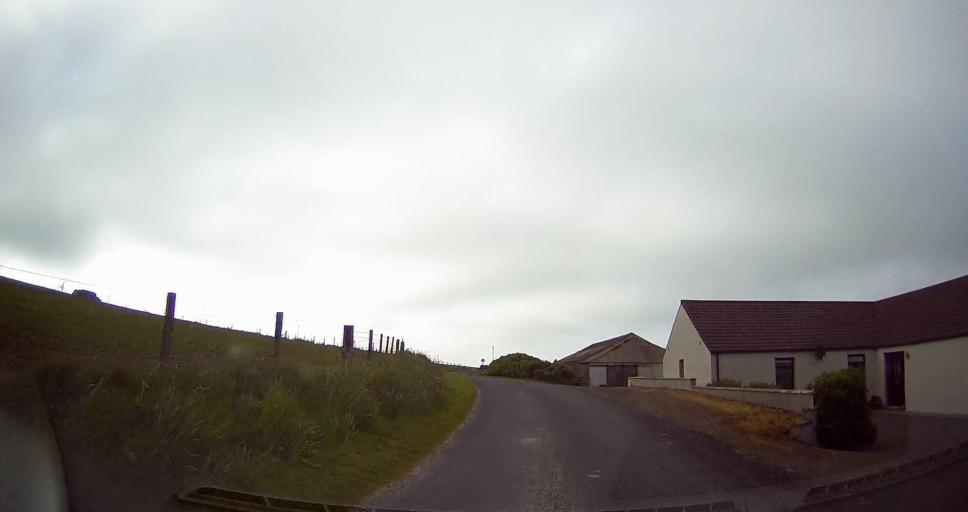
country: GB
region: Scotland
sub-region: Orkney Islands
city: Orkney
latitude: 59.1198
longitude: -3.1336
